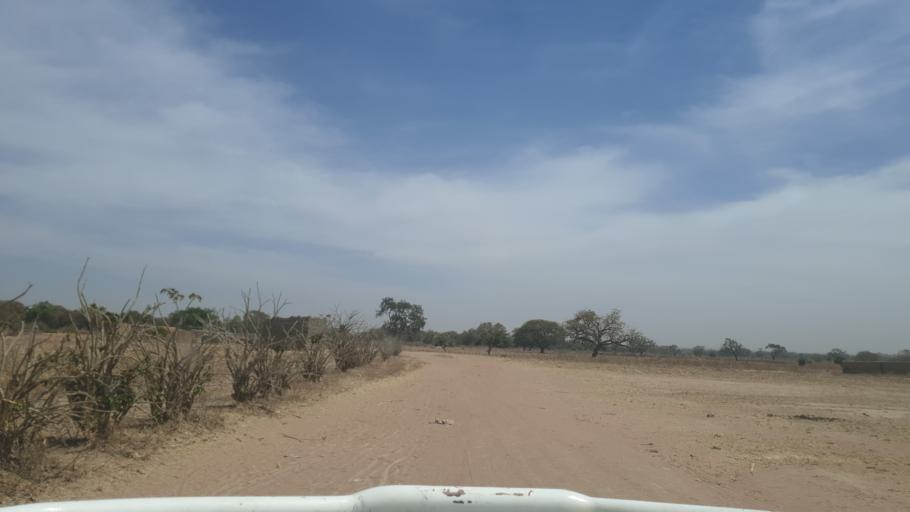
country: ML
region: Sikasso
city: Yorosso
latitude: 12.2941
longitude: -4.6445
